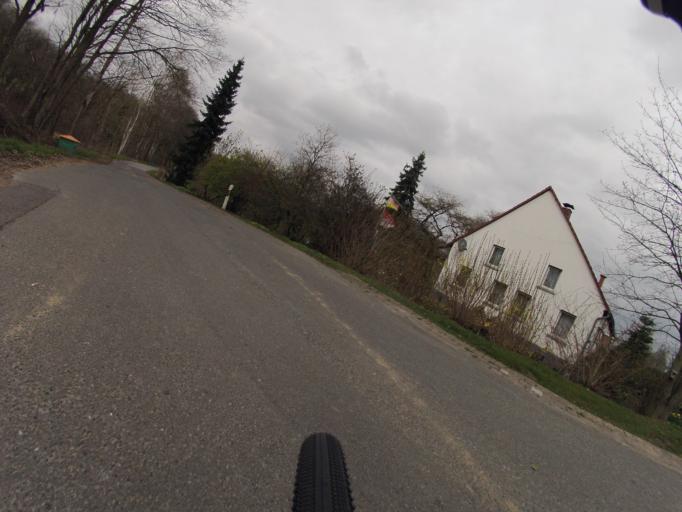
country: DE
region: North Rhine-Westphalia
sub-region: Regierungsbezirk Munster
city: Tecklenburg
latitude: 52.2750
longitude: 7.8337
